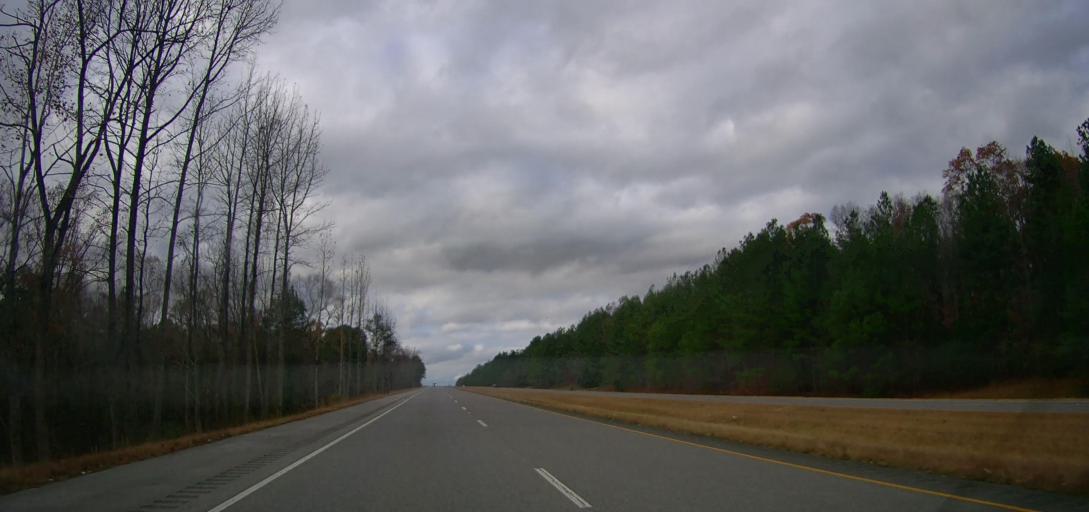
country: US
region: Alabama
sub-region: Lawrence County
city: Town Creek
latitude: 34.6168
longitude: -87.4639
